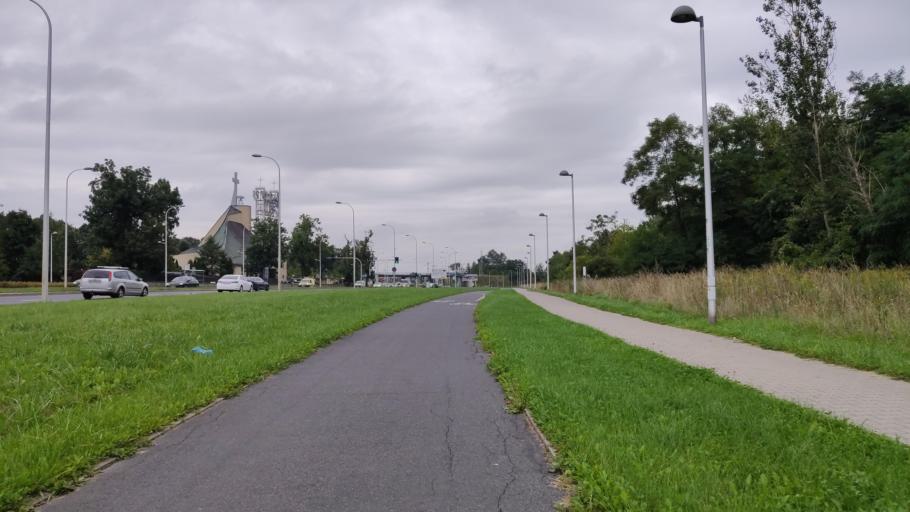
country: PL
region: Lower Silesian Voivodeship
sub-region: Powiat wroclawski
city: Wroclaw
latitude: 51.0741
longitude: 17.0527
